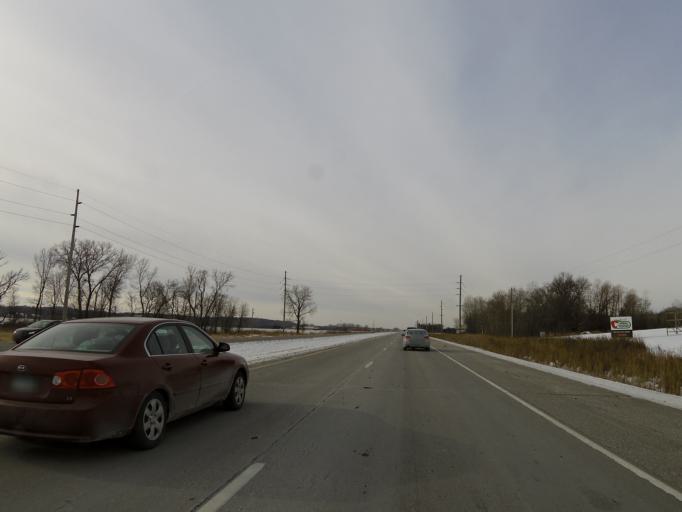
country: US
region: Minnesota
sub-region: Scott County
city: Jordan
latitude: 44.6609
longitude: -93.6659
